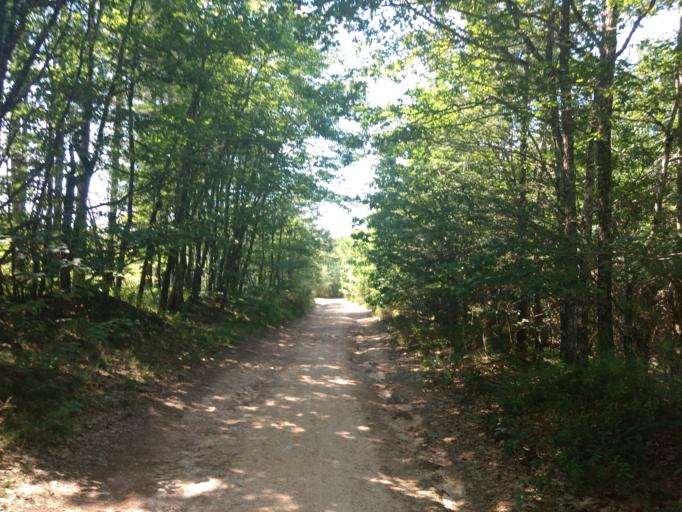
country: FR
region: Midi-Pyrenees
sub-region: Departement de l'Aveyron
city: Laissac
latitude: 44.3655
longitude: 2.7560
